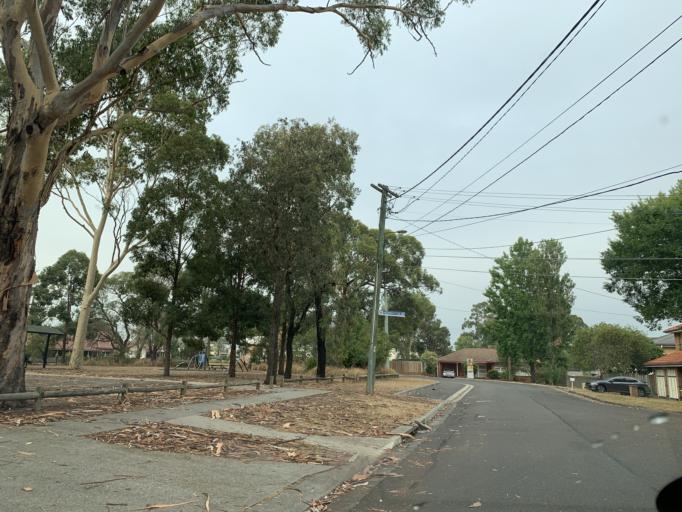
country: AU
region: New South Wales
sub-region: Parramatta
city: Dundas Valley
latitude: -33.7766
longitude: 151.0648
